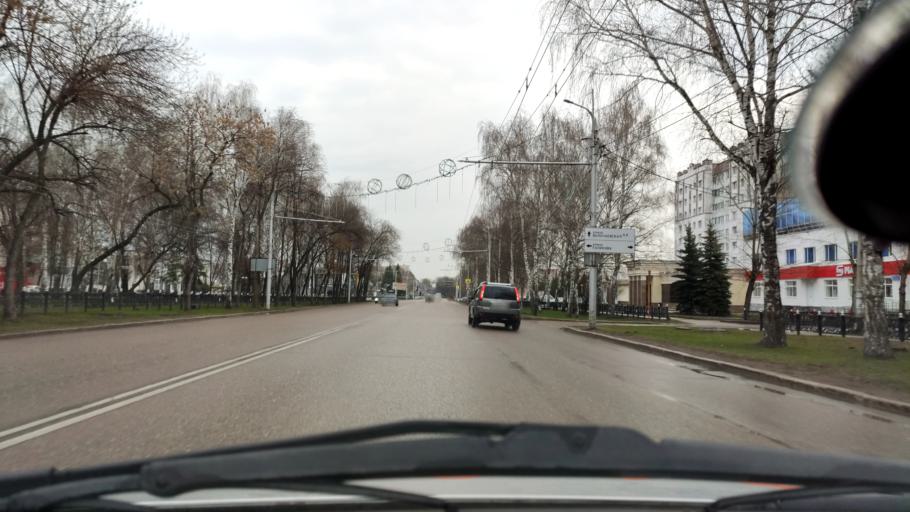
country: RU
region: Bashkortostan
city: Sterlitamak
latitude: 53.6348
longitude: 55.9348
